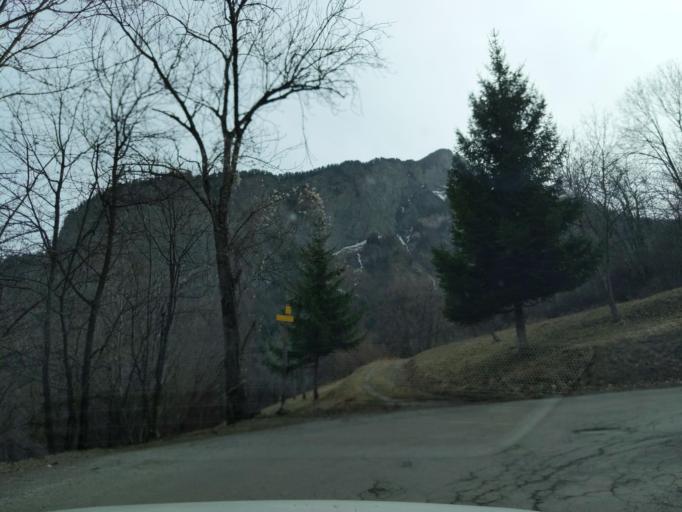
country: FR
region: Rhone-Alpes
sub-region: Departement de la Savoie
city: Villargondran
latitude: 45.2554
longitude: 6.3667
